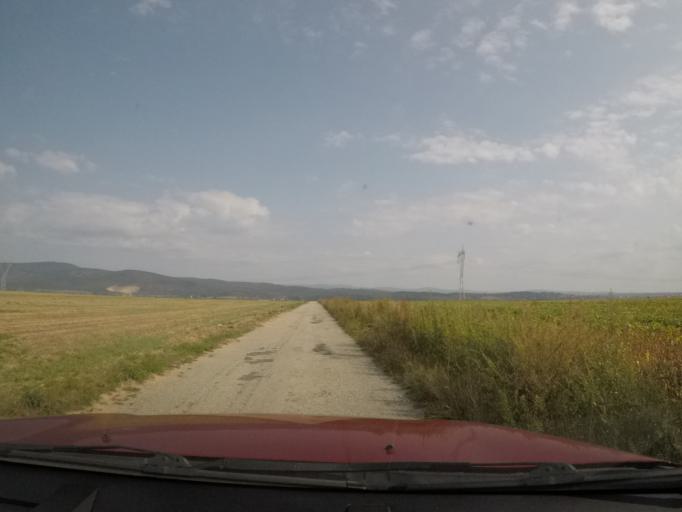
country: SK
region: Kosicky
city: Moldava nad Bodvou
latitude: 48.5848
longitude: 20.9569
